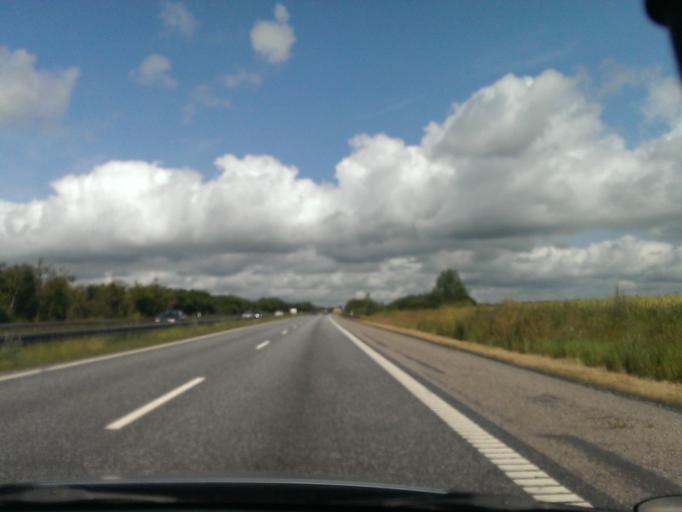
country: DK
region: North Denmark
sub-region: Mariagerfjord Kommune
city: Hobro
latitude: 56.7264
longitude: 9.7128
